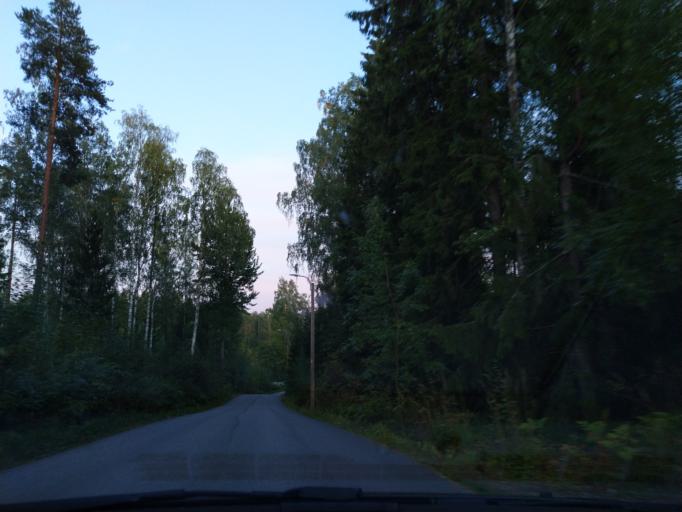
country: FI
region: Uusimaa
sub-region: Helsinki
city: Tuusula
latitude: 60.3622
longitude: 25.0592
